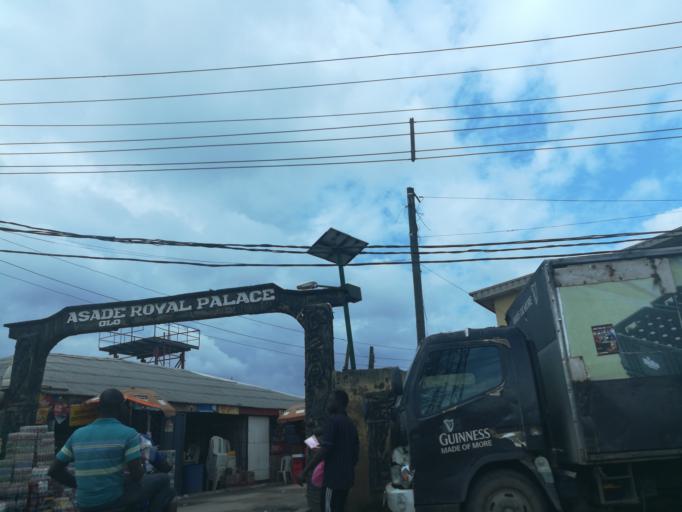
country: NG
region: Lagos
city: Agege
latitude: 6.6176
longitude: 3.3342
